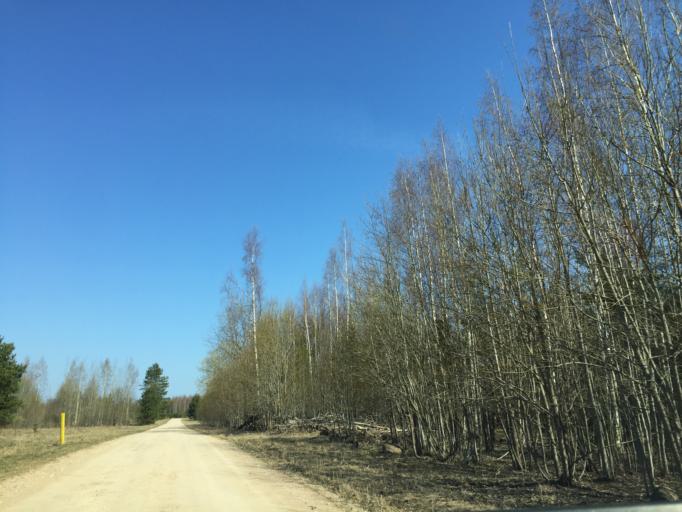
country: EE
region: Tartu
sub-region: Alatskivi vald
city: Kallaste
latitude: 58.5332
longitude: 26.9447
